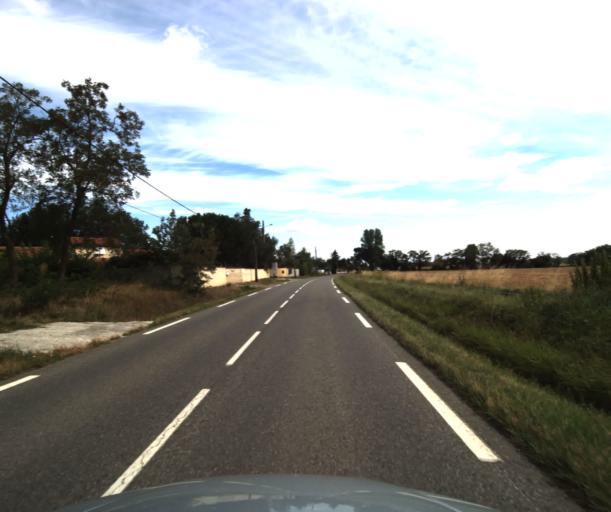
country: FR
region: Midi-Pyrenees
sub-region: Departement de la Haute-Garonne
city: Seysses
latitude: 43.4800
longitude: 1.3046
